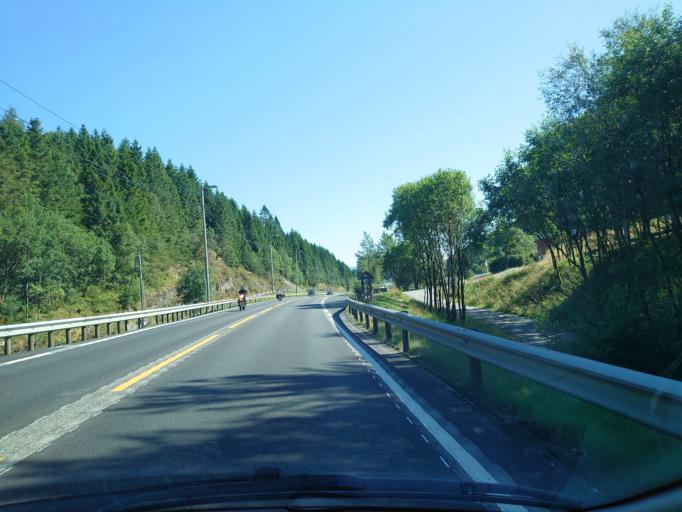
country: NO
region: Hordaland
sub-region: Bergen
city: Hylkje
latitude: 60.4725
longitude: 5.3628
